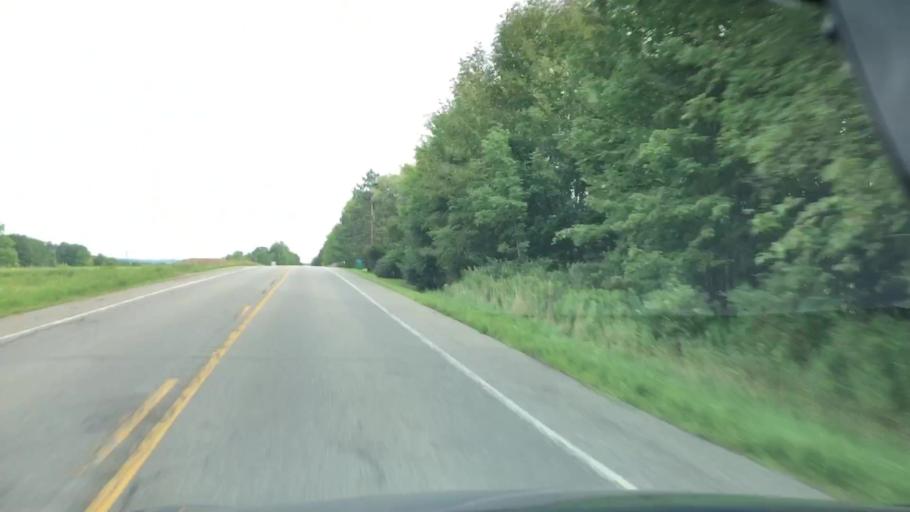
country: US
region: Pennsylvania
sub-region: Erie County
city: Union City
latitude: 41.8096
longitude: -79.8004
